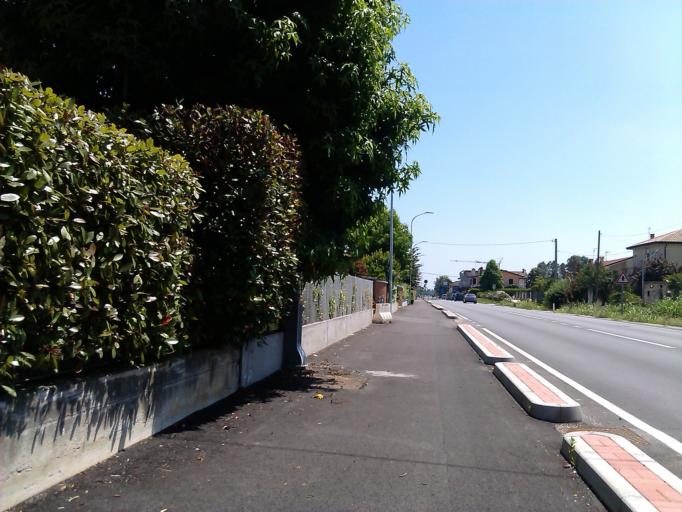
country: IT
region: Veneto
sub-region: Provincia di Padova
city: Camposampiero
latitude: 45.5577
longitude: 11.9629
